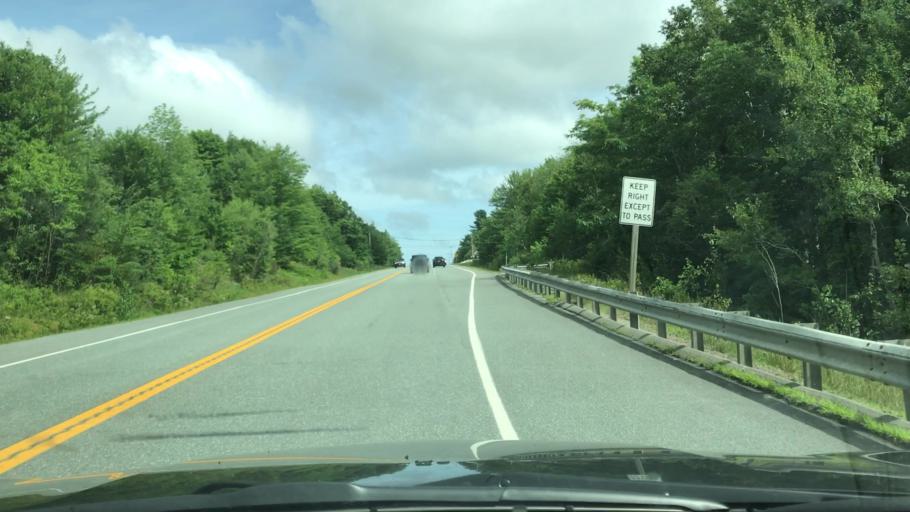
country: US
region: Maine
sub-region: Hancock County
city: Surry
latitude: 44.5554
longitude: -68.5408
